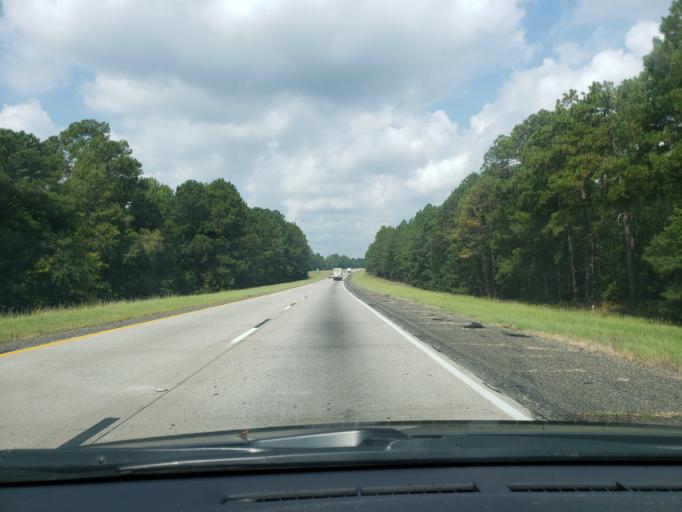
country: US
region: Georgia
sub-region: Treutlen County
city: Soperton
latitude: 32.4353
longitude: -82.6497
